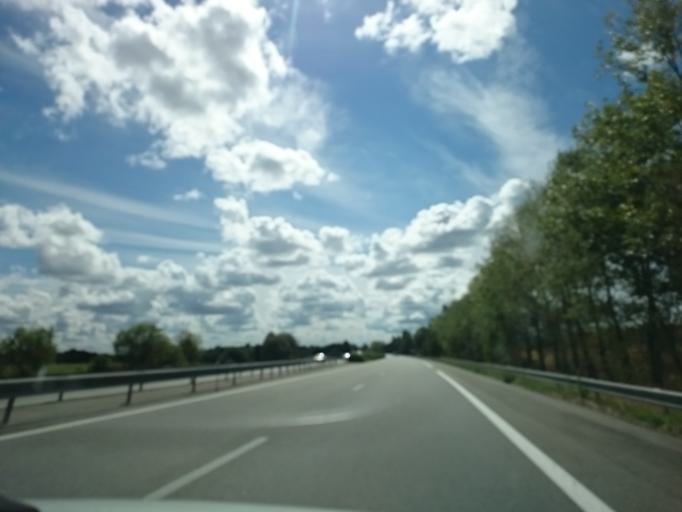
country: FR
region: Pays de la Loire
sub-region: Departement de la Loire-Atlantique
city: Saint-Mars-du-Desert
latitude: 47.3336
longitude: -1.3957
